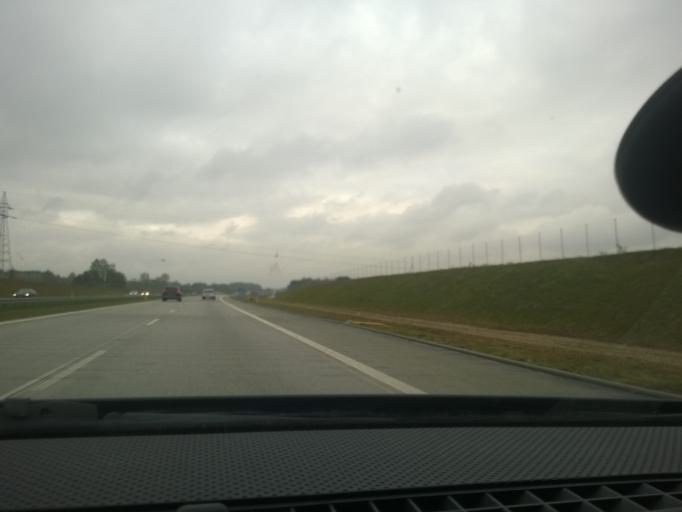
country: PL
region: Lodz Voivodeship
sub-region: Powiat lodzki wschodni
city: Andrespol
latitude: 51.7696
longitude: 19.5993
